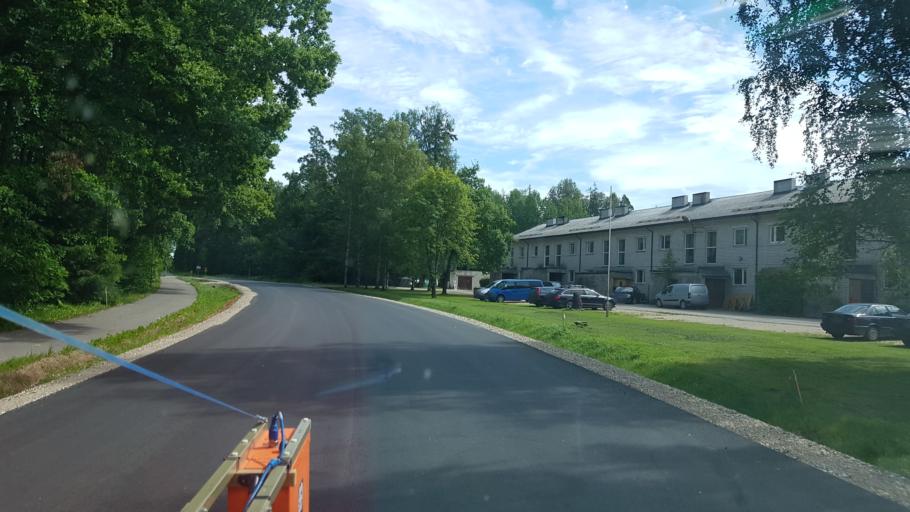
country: EE
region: Viljandimaa
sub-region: Suure-Jaani vald
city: Suure-Jaani
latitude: 58.5386
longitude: 25.4984
